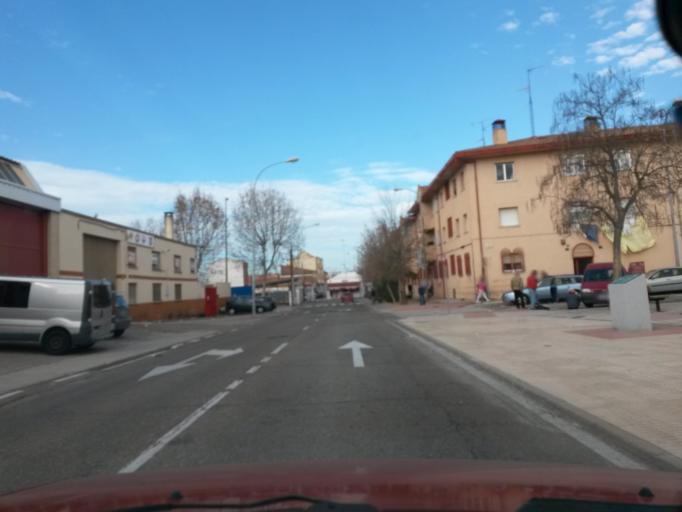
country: ES
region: Castille and Leon
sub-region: Provincia de Salamanca
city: Salamanca
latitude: 40.9730
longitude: -5.6396
